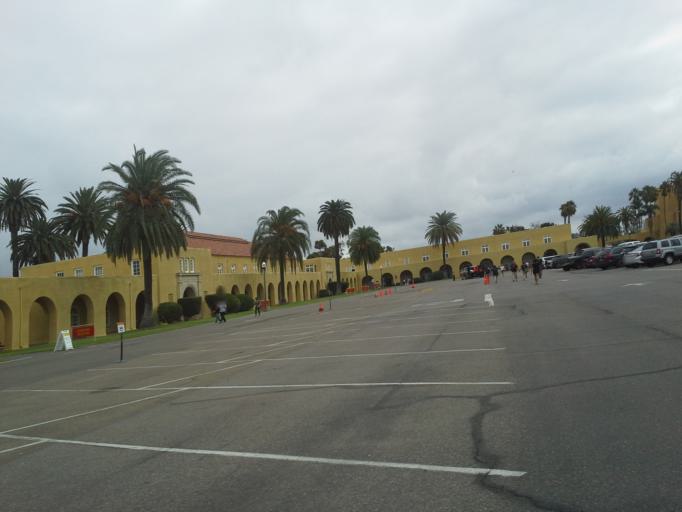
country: US
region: California
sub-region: San Diego County
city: San Diego
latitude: 32.7418
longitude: -117.1951
